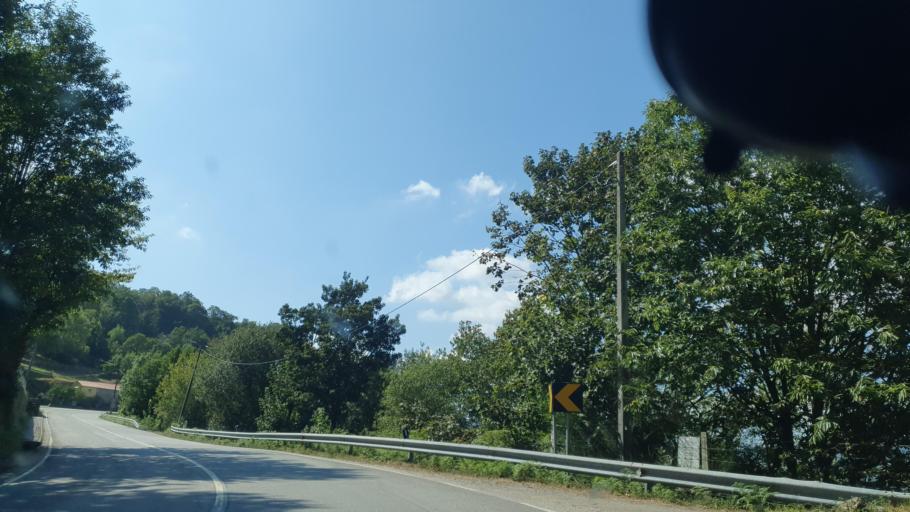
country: PT
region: Braga
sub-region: Vieira do Minho
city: Vieira do Minho
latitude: 41.6728
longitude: -8.1422
